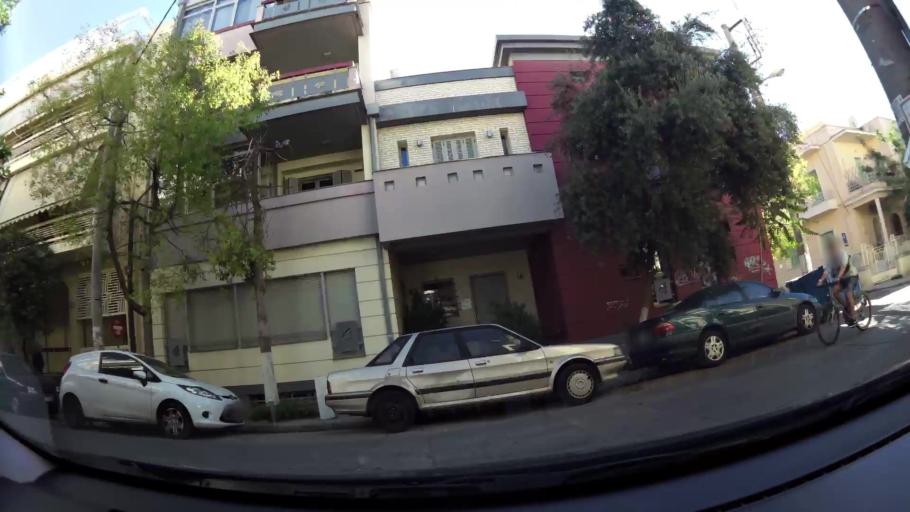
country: GR
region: Attica
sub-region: Nomarchia Athinas
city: Khalandrion
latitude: 38.0190
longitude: 23.7987
